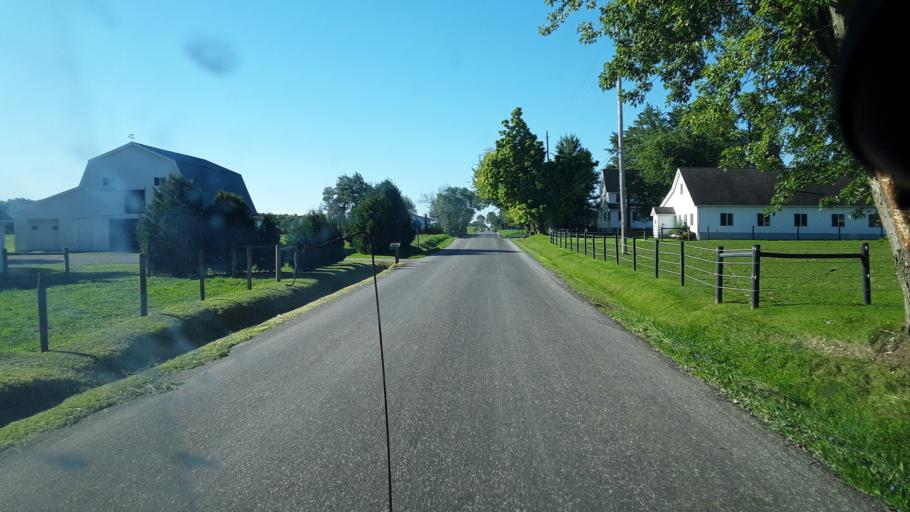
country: US
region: Ohio
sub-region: Geauga County
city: Middlefield
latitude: 41.4751
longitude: -81.0033
